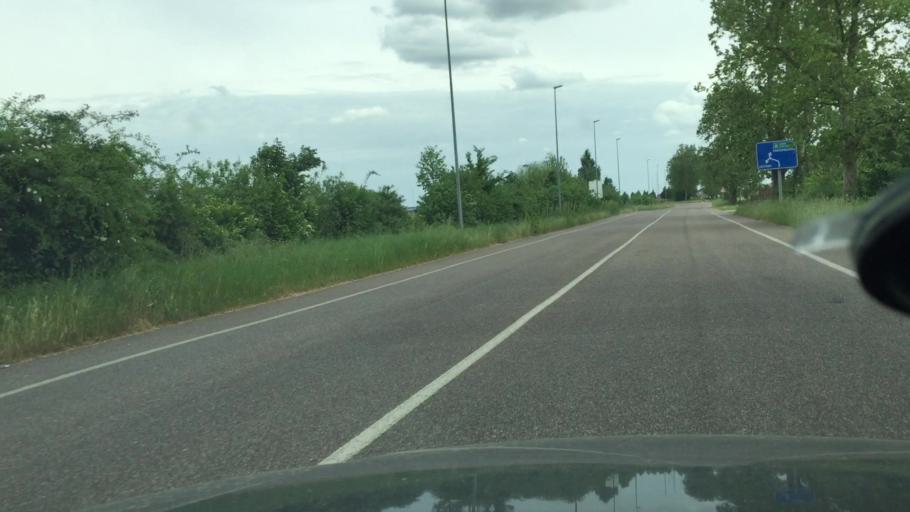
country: IT
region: Emilia-Romagna
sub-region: Provincia di Ferrara
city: Cona
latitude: 44.7996
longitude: 11.7183
